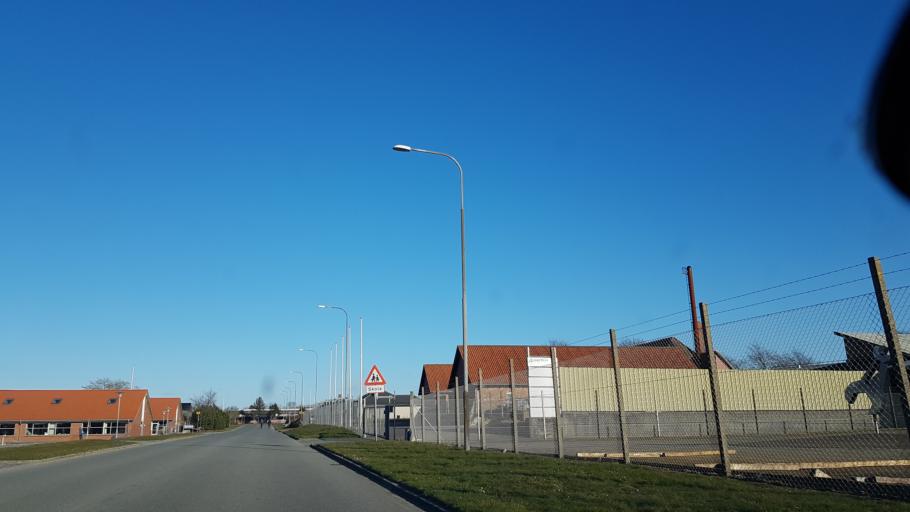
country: DK
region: South Denmark
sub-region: Esbjerg Kommune
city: Esbjerg
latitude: 55.5095
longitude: 8.4132
